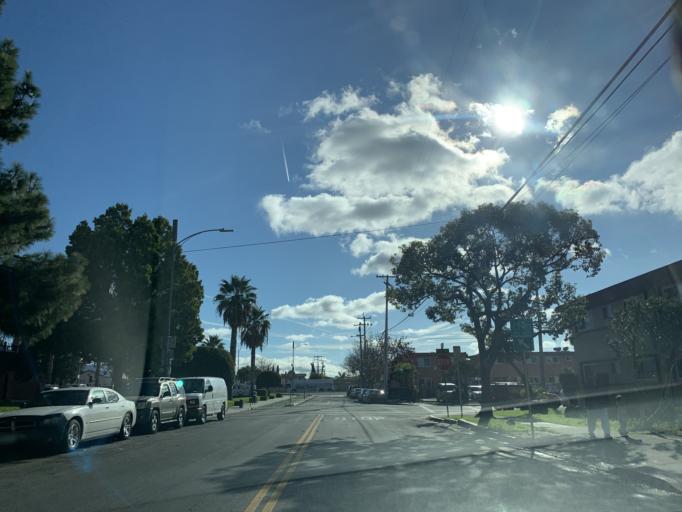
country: US
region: California
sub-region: Santa Clara County
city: Alum Rock
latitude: 37.3444
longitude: -121.8389
